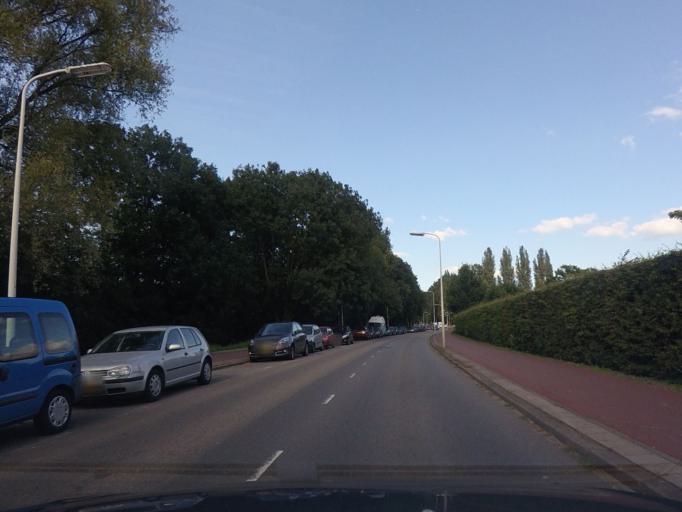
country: NL
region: South Holland
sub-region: Gemeente Leidschendam-Voorburg
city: Voorburg
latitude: 52.0850
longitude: 4.3510
